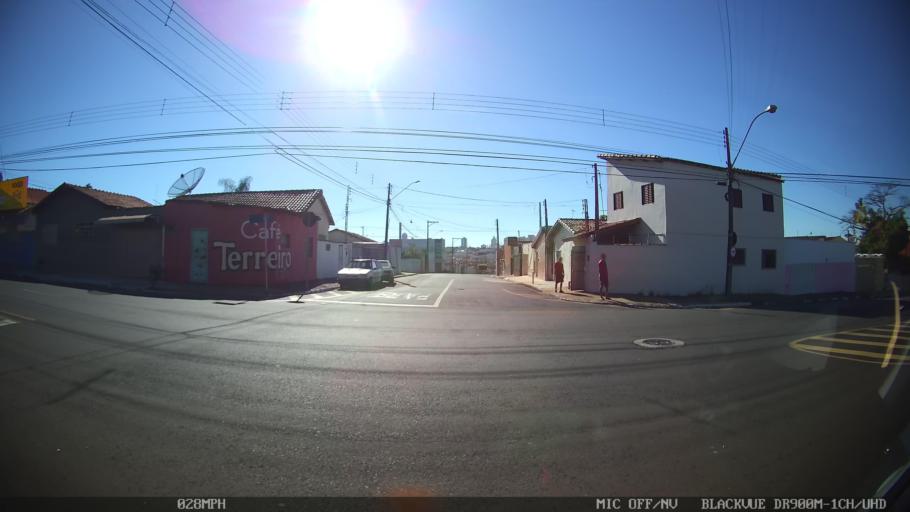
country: BR
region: Sao Paulo
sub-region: Franca
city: Franca
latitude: -20.5419
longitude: -47.4132
